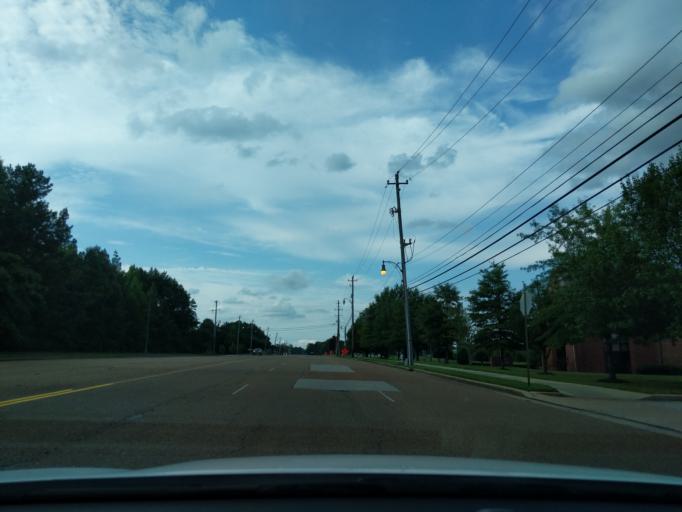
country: US
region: Tennessee
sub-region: Shelby County
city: Germantown
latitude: 35.0405
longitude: -89.7597
